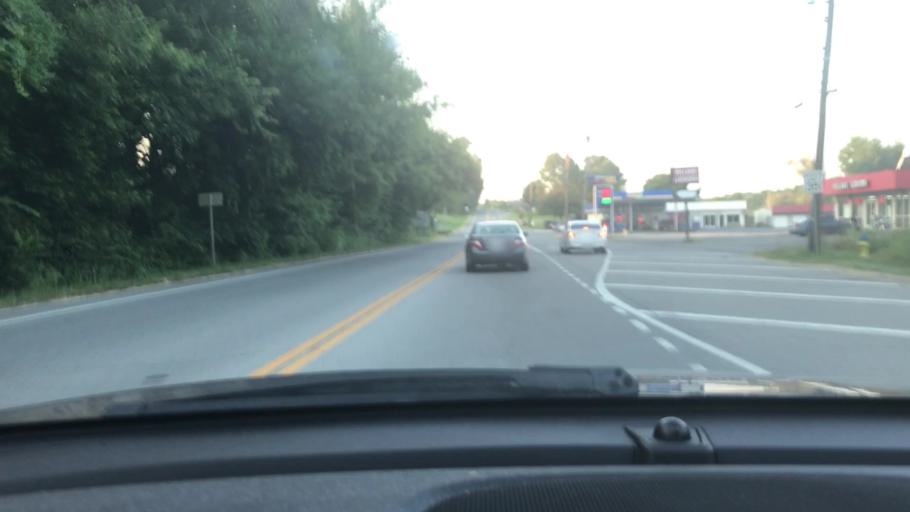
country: US
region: Tennessee
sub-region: Dickson County
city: Dickson
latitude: 36.0848
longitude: -87.3789
